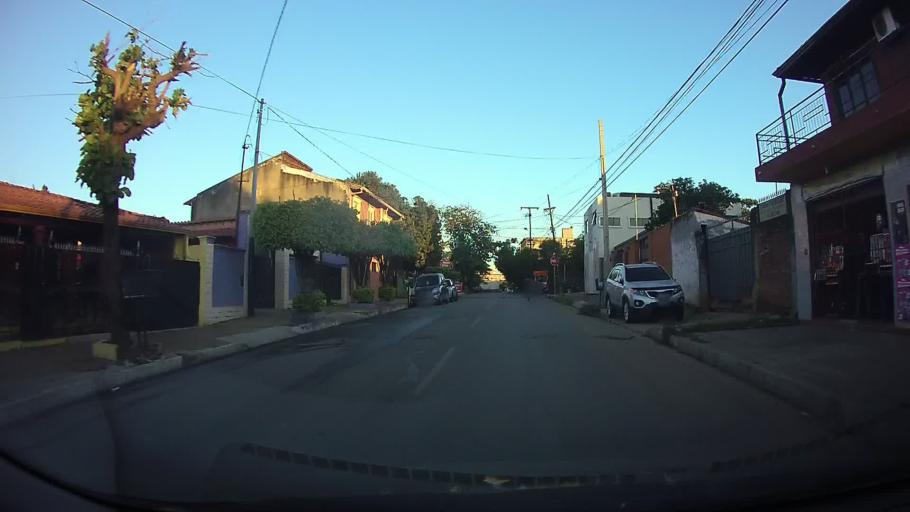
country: PY
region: Central
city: Fernando de la Mora
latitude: -25.3249
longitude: -57.5490
